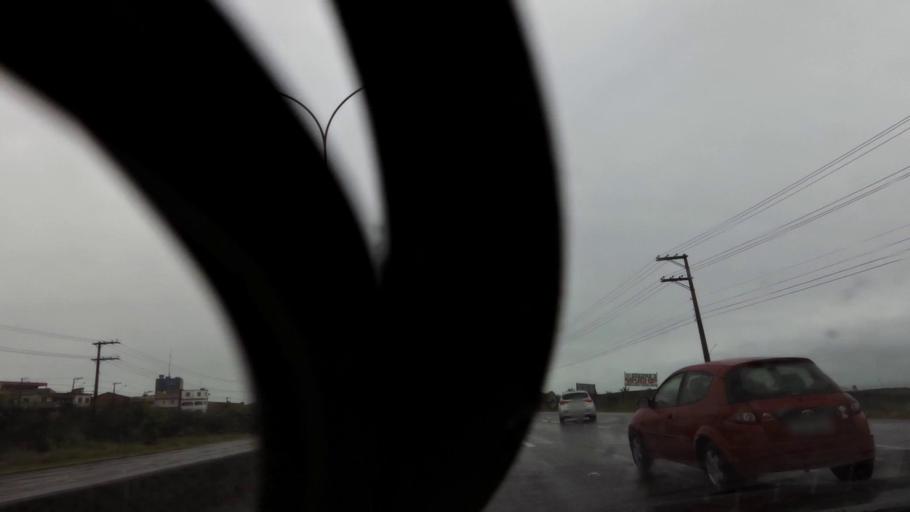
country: BR
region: Espirito Santo
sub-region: Vila Velha
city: Vila Velha
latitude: -20.4513
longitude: -40.3352
